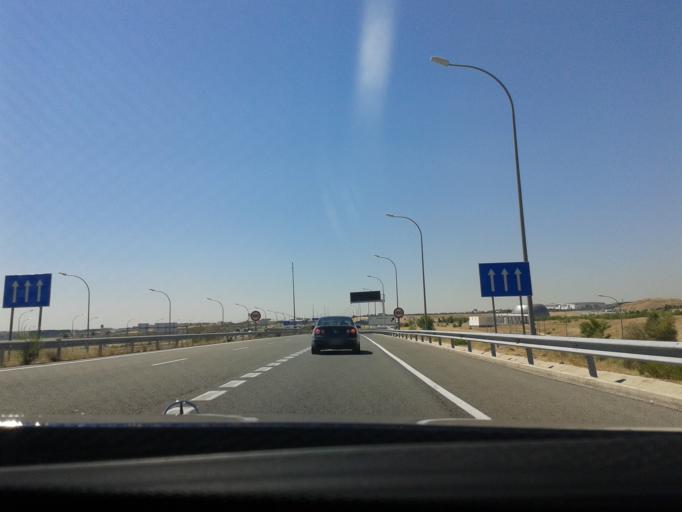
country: ES
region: Madrid
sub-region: Provincia de Madrid
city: Barajas de Madrid
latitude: 40.4916
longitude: -3.6024
